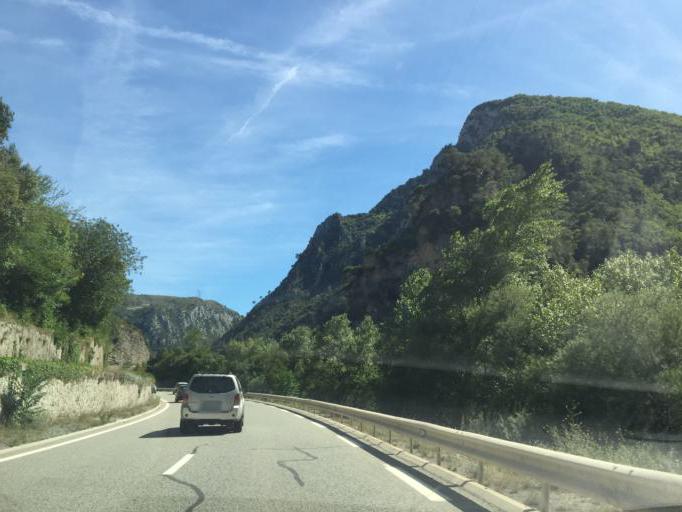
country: FR
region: Provence-Alpes-Cote d'Azur
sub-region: Departement des Alpes-Maritimes
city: Gilette
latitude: 43.8798
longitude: 7.1898
